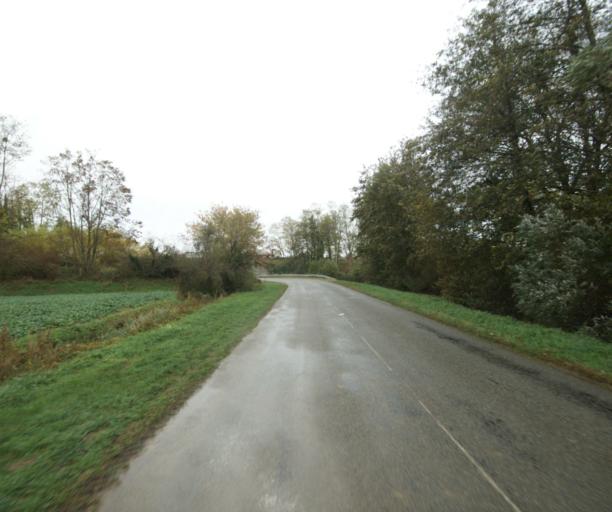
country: FR
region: Rhone-Alpes
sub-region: Departement de l'Ain
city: Pont-de-Vaux
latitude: 46.4765
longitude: 4.8885
